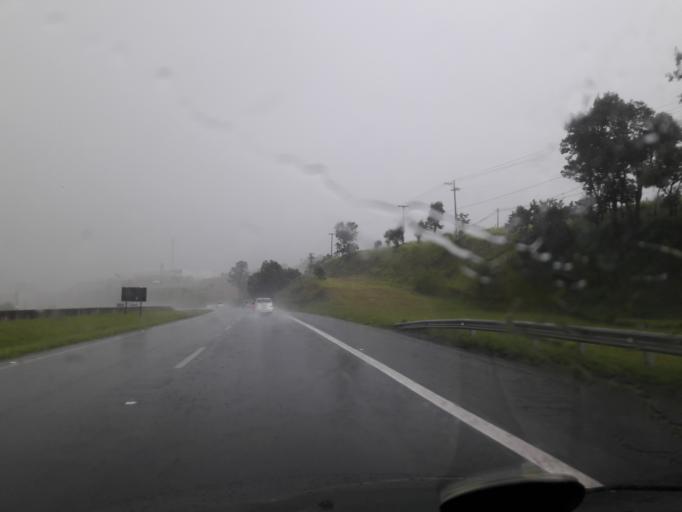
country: BR
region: Sao Paulo
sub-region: Bom Jesus Dos Perdoes
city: Bom Jesus dos Perdoes
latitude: -23.1668
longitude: -46.4445
